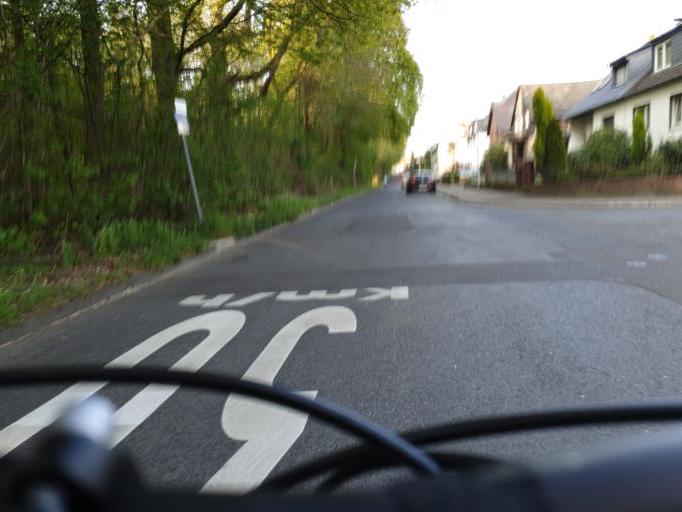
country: DE
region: North Rhine-Westphalia
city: Opladen
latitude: 51.0461
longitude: 7.0470
